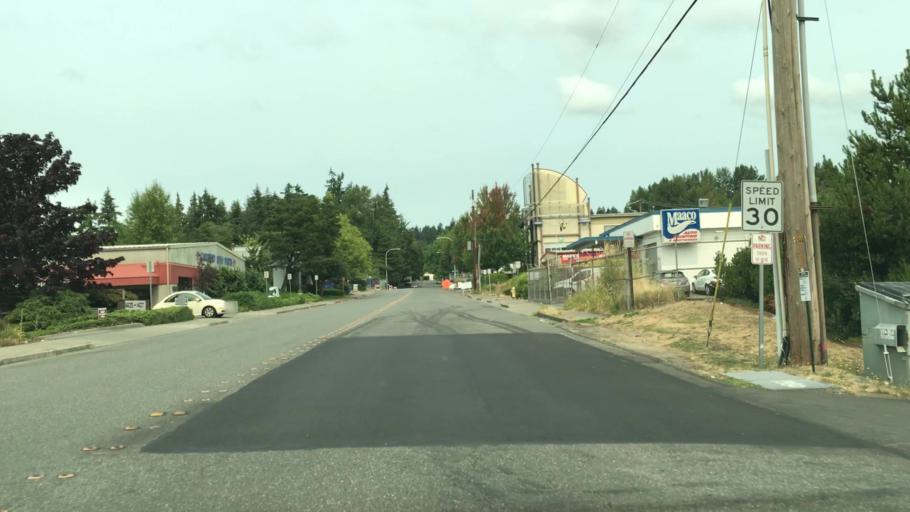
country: US
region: Washington
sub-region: King County
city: Bellevue
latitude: 47.6228
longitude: -122.1644
